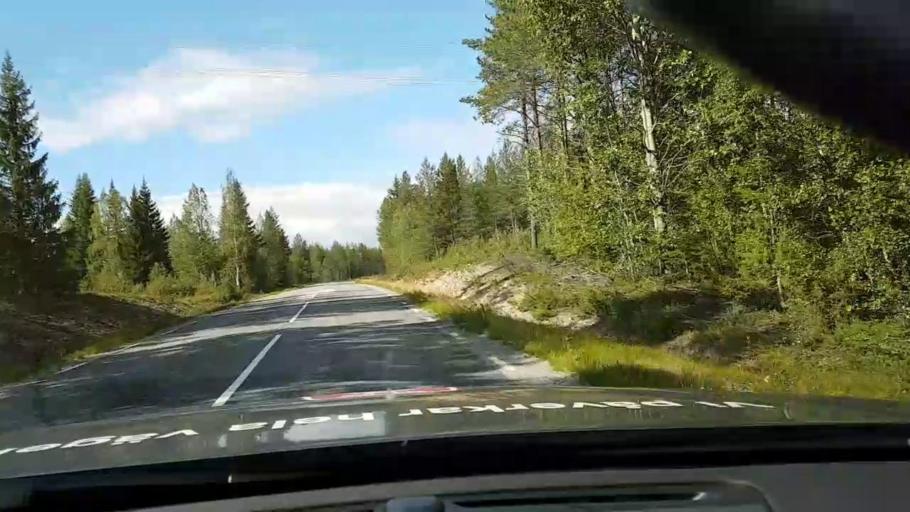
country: SE
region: Vaesterbotten
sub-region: Asele Kommun
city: Asele
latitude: 63.8170
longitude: 17.4963
